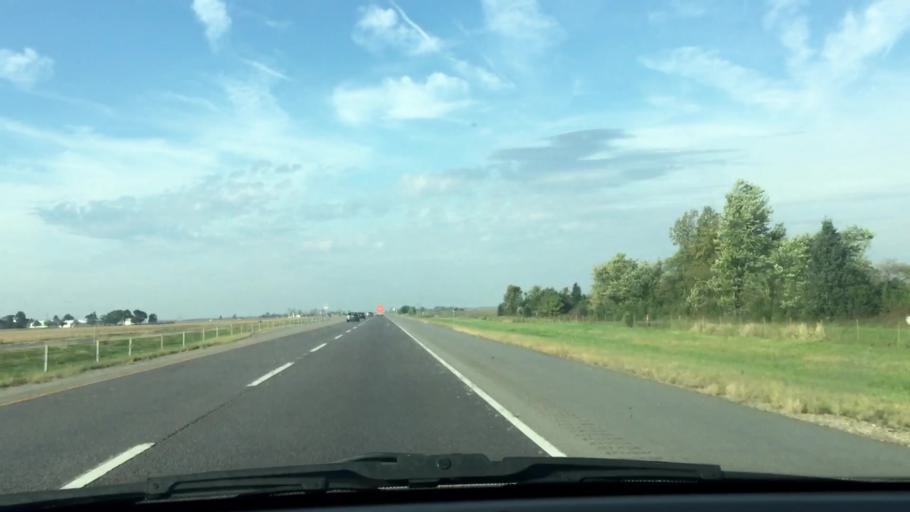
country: US
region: Illinois
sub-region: Lee County
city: Franklin Grove
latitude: 41.8509
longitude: -89.2321
